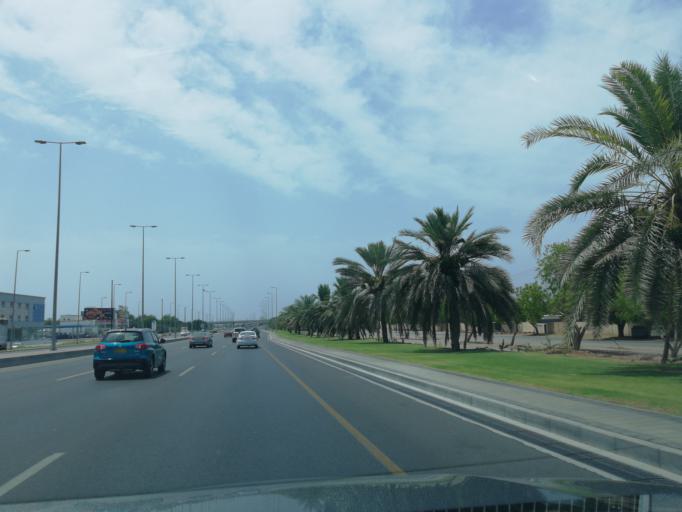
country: OM
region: Muhafazat Masqat
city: As Sib al Jadidah
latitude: 23.6725
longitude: 58.1438
